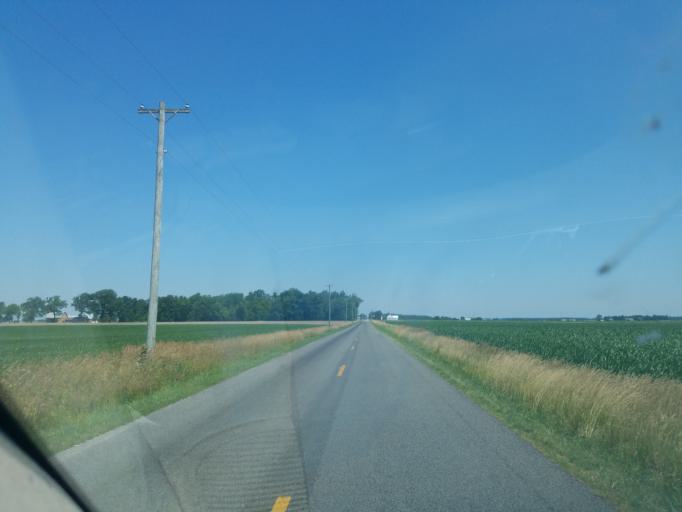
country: US
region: Ohio
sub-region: Mercer County
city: Rockford
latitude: 40.6514
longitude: -84.7086
